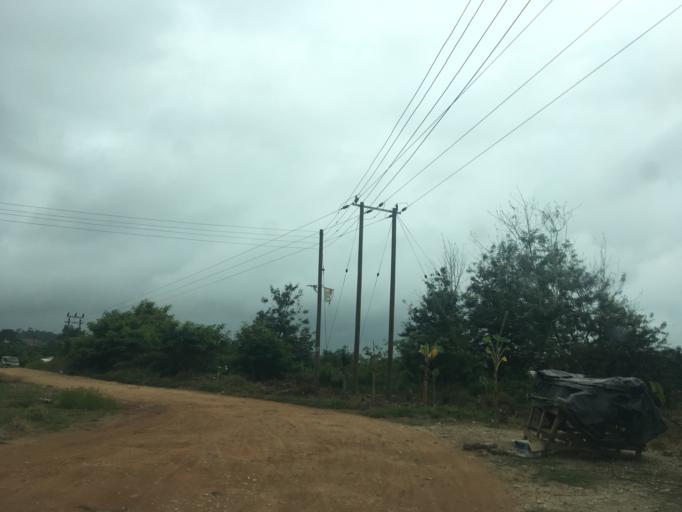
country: GH
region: Western
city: Wassa-Akropong
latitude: 5.8166
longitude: -2.4330
